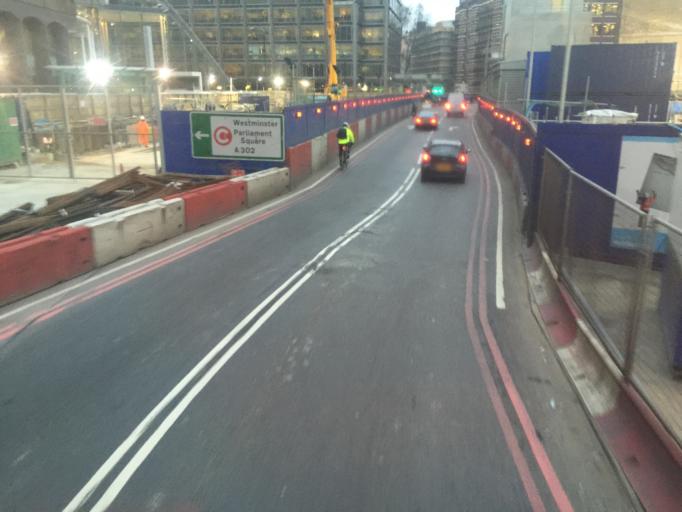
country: GB
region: England
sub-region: Greater London
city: London
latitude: 51.4976
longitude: -0.1423
